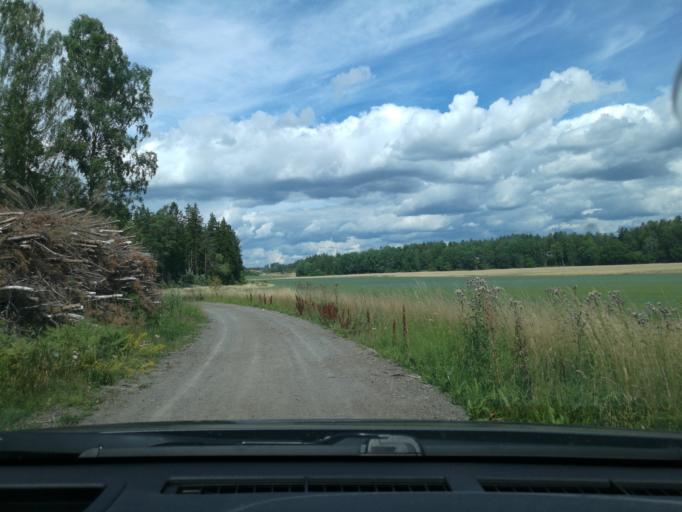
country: SE
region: Stockholm
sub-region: Sigtuna Kommun
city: Marsta
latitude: 59.6089
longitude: 17.8024
